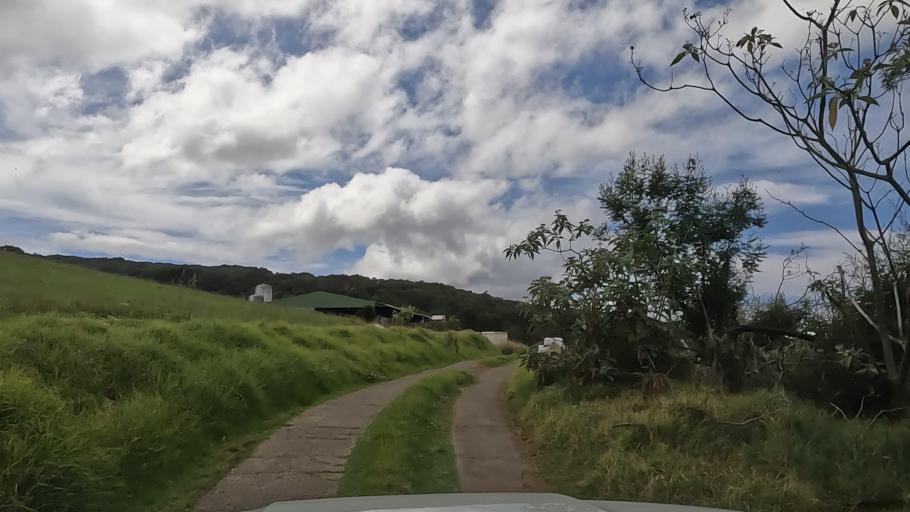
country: RE
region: Reunion
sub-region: Reunion
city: Le Tampon
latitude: -21.2372
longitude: 55.5798
